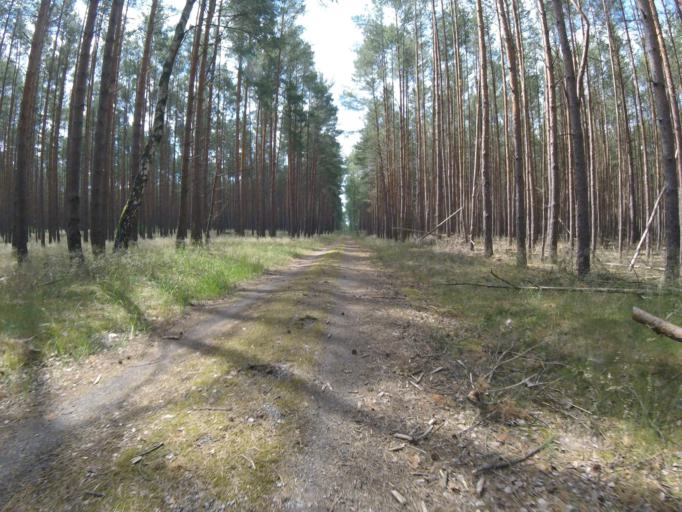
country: DE
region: Brandenburg
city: Halbe
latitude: 52.1284
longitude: 13.6734
